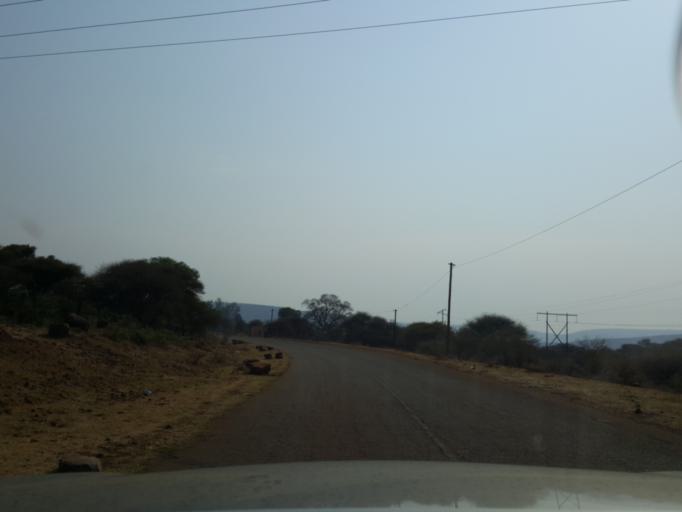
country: BW
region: South East
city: Lobatse
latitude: -25.3239
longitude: 25.7929
